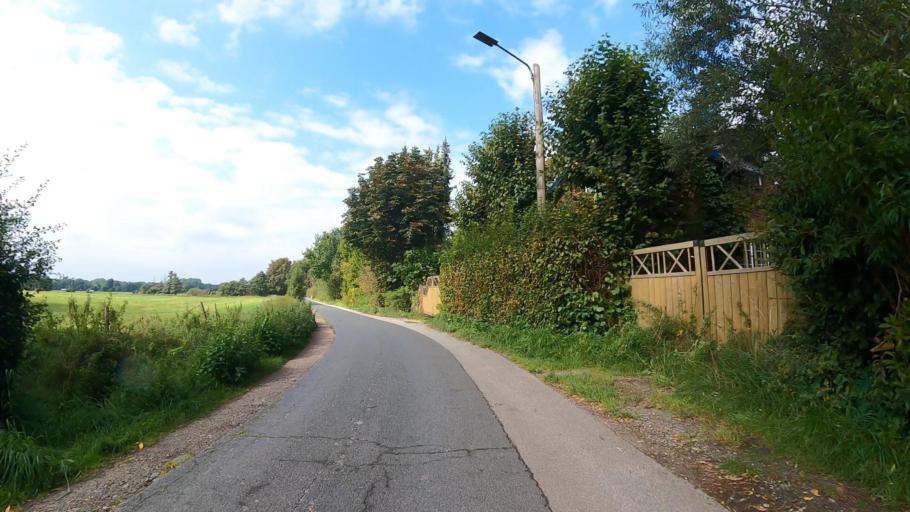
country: DE
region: Schleswig-Holstein
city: Tornesch
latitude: 53.7204
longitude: 9.7016
